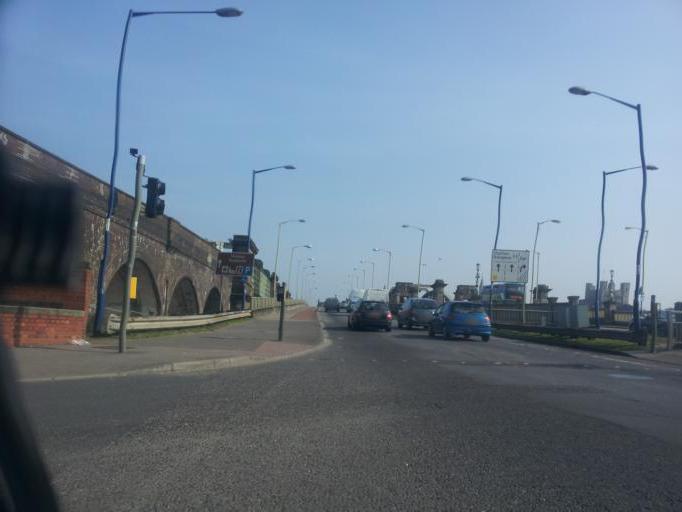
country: GB
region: England
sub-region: Kent
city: Strood
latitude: 51.3936
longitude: 0.4991
